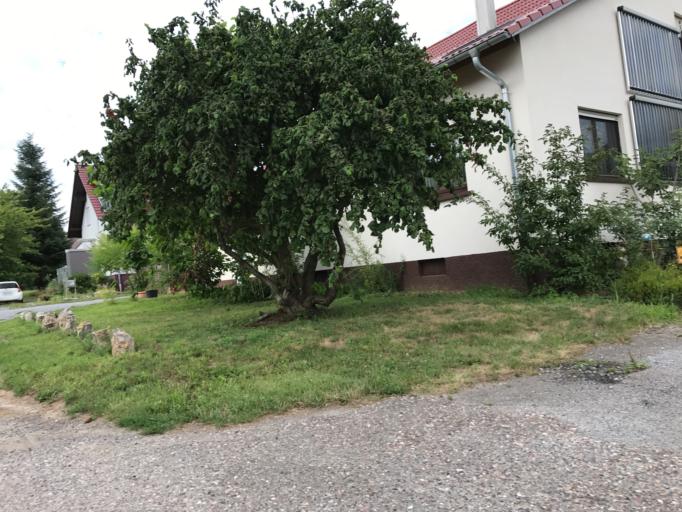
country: DE
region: Baden-Wuerttemberg
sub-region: Karlsruhe Region
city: Joehlingen
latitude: 49.0519
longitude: 8.5796
